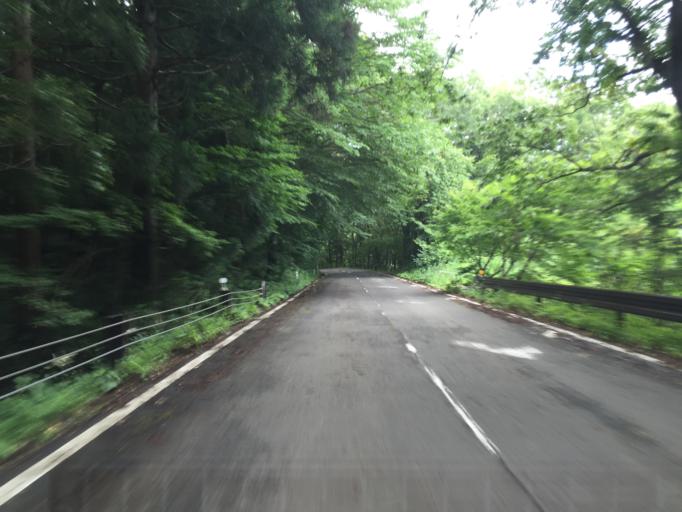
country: JP
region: Fukushima
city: Nihommatsu
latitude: 37.6770
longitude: 140.3353
